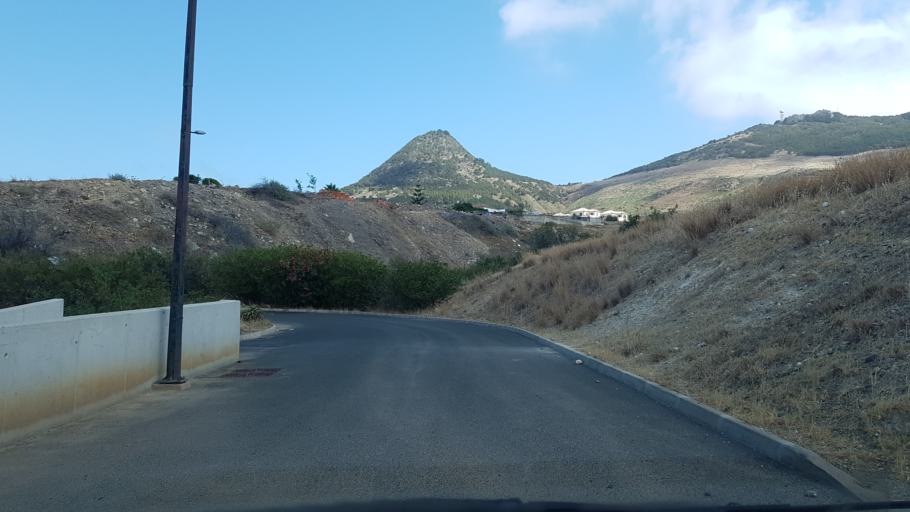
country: PT
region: Madeira
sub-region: Porto Santo
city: Vila de Porto Santo
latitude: 33.0653
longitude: -16.3268
